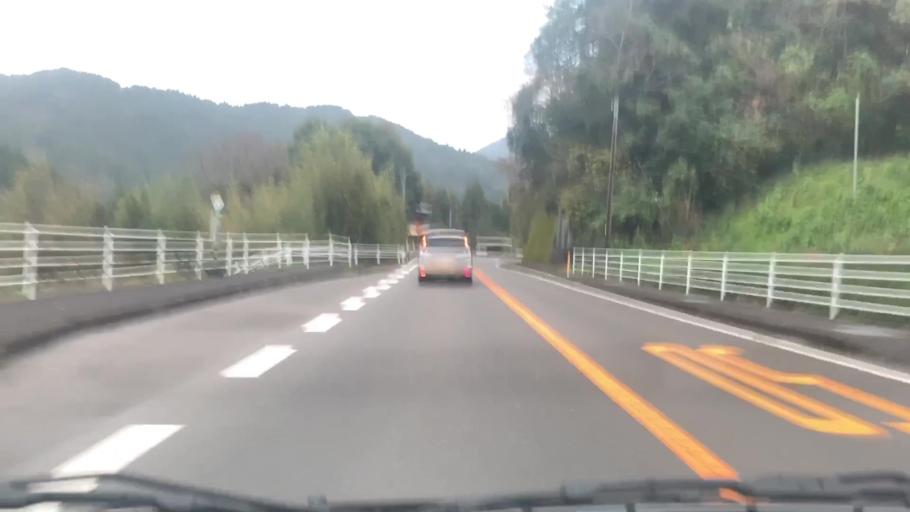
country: JP
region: Saga Prefecture
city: Ureshinomachi-shimojuku
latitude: 33.0591
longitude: 129.9486
